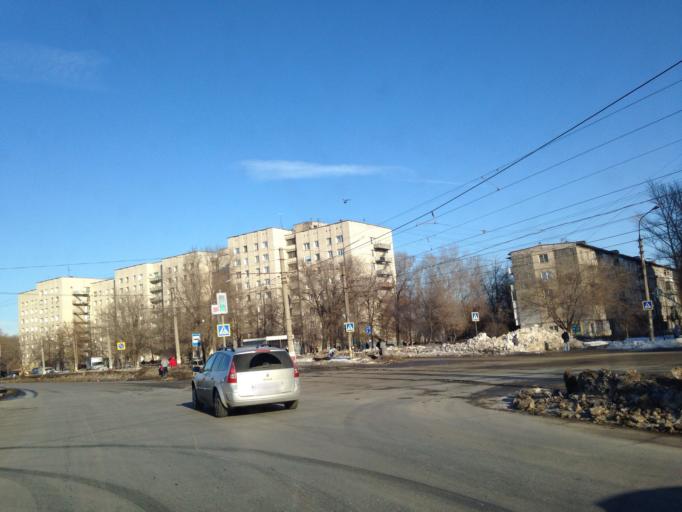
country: RU
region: Ulyanovsk
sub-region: Ulyanovskiy Rayon
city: Ulyanovsk
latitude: 54.3154
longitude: 48.3561
